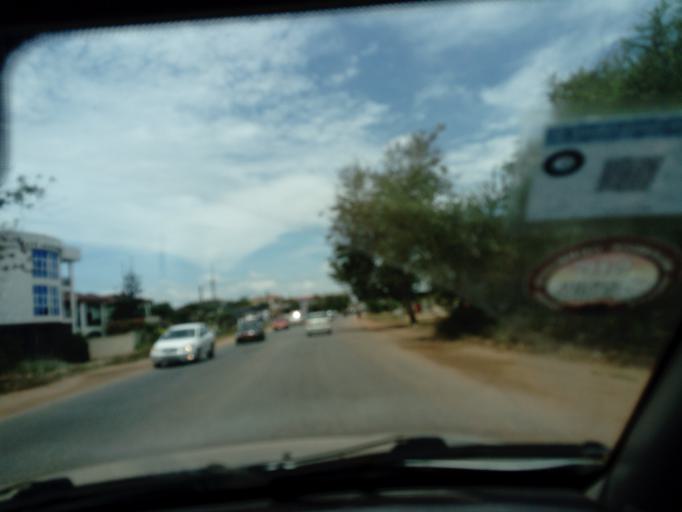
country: GH
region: Central
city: Cape Coast
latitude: 5.1375
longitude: -1.2796
